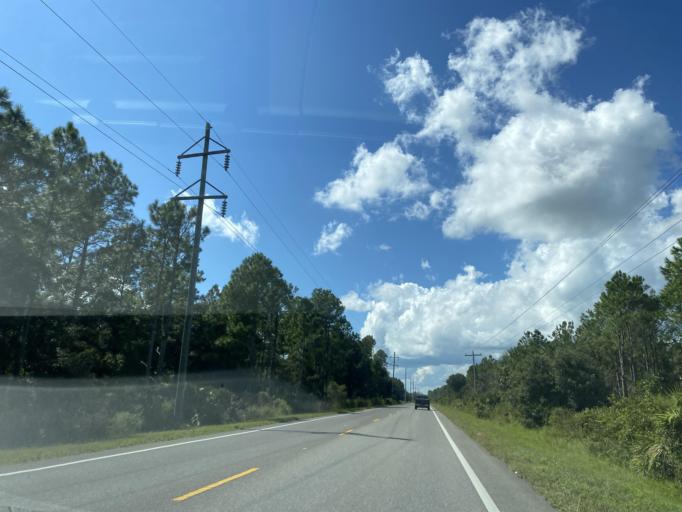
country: US
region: Florida
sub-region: Lake County
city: Umatilla
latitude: 28.9603
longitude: -81.6079
